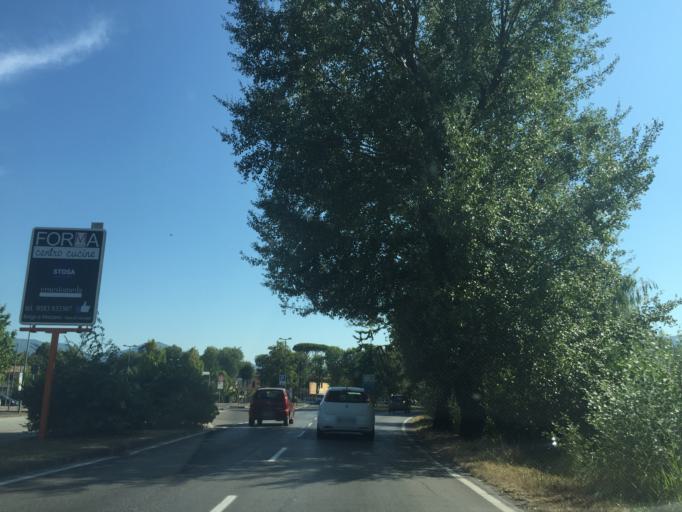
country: IT
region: Tuscany
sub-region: Provincia di Lucca
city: Lucca
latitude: 43.8469
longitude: 10.4945
